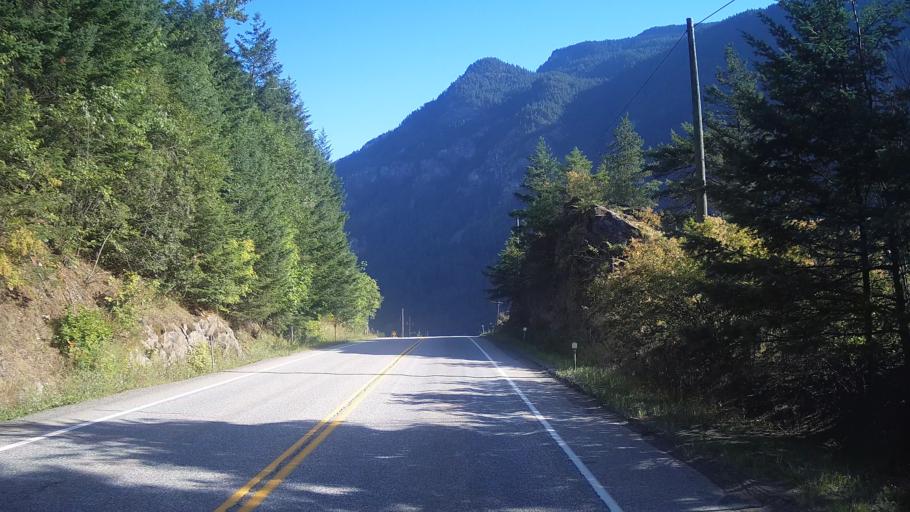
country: CA
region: British Columbia
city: Hope
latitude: 49.5750
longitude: -121.4032
